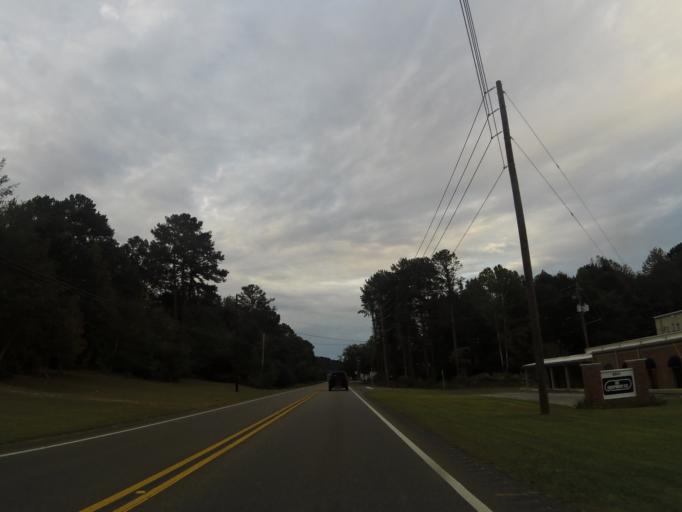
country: US
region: Alabama
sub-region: Jefferson County
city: Trussville
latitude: 33.6299
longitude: -86.5899
